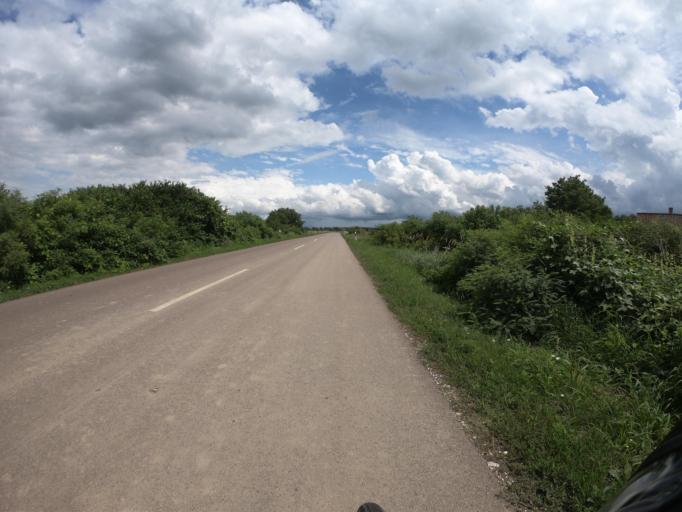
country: HU
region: Jasz-Nagykun-Szolnok
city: Tiszafured
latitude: 47.6908
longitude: 20.7899
